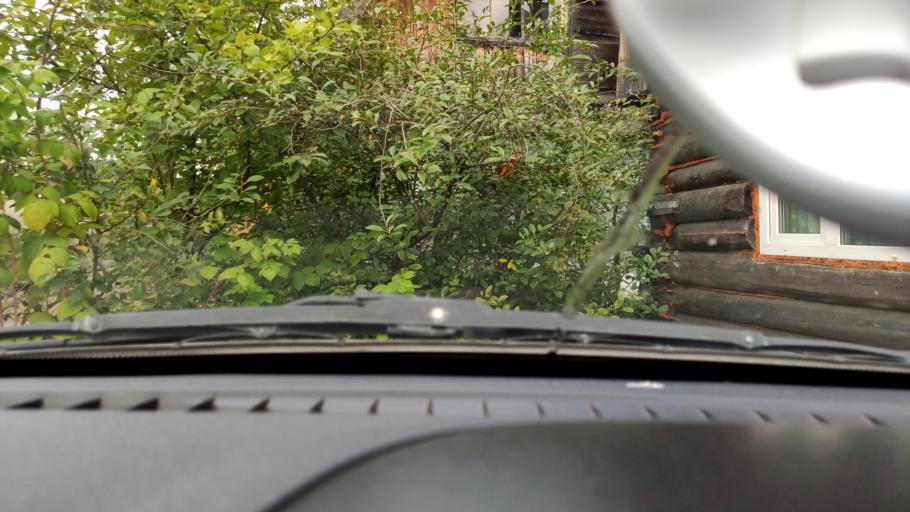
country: RU
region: Perm
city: Overyata
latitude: 58.0187
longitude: 55.9657
